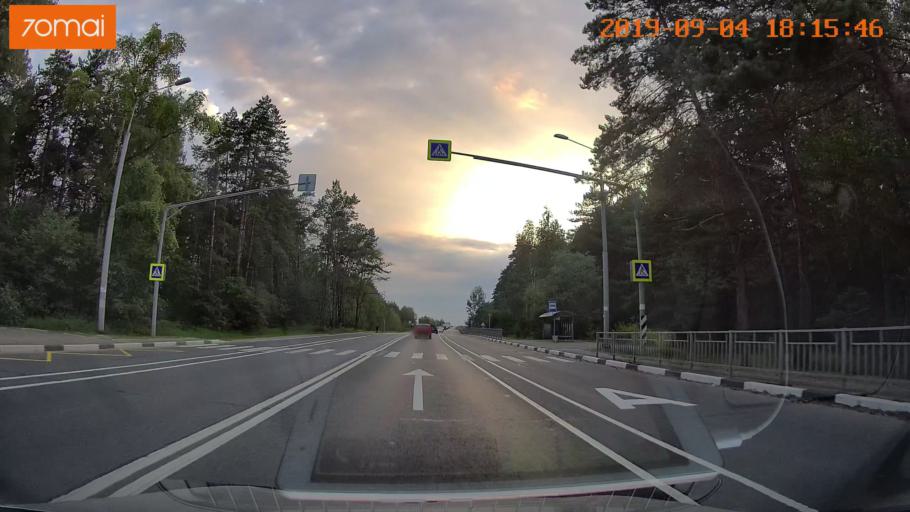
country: RU
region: Moskovskaya
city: Lopatinskiy
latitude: 55.3452
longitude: 38.6965
